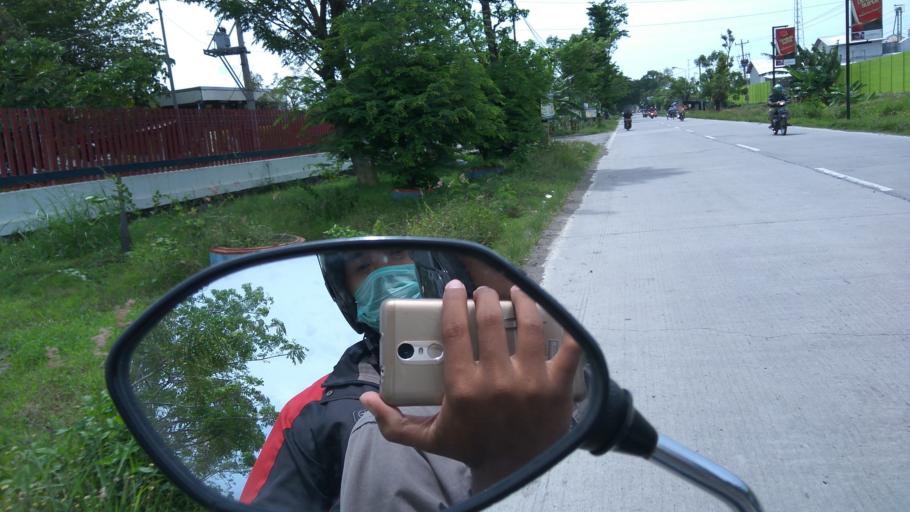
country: ID
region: Central Java
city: Mranggen
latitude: -7.0469
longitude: 110.5869
